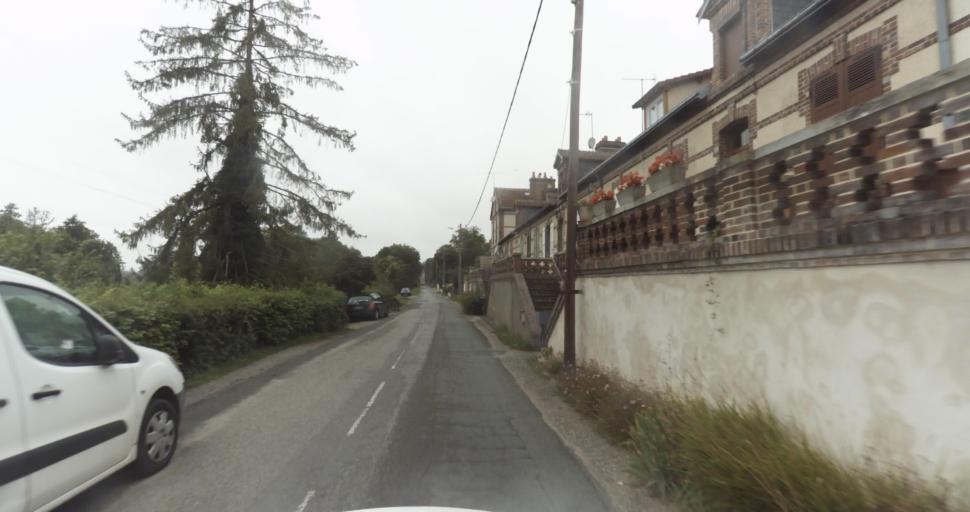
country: FR
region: Centre
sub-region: Departement d'Eure-et-Loir
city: Vert-en-Drouais
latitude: 48.7674
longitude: 1.3044
